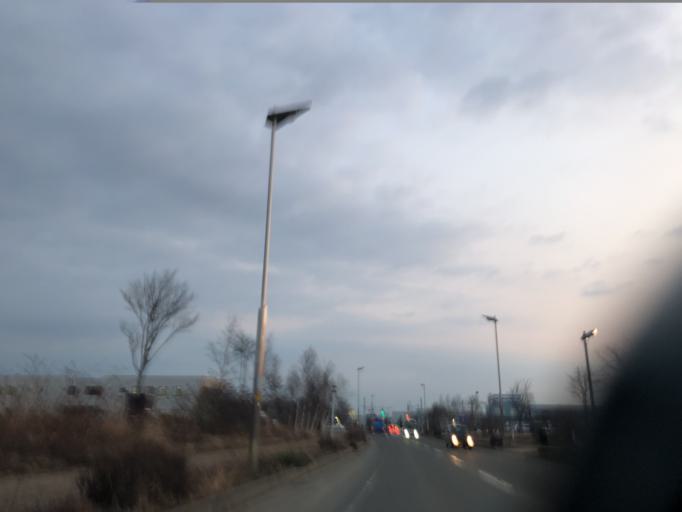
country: JP
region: Hokkaido
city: Chitose
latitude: 42.8156
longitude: 141.6790
